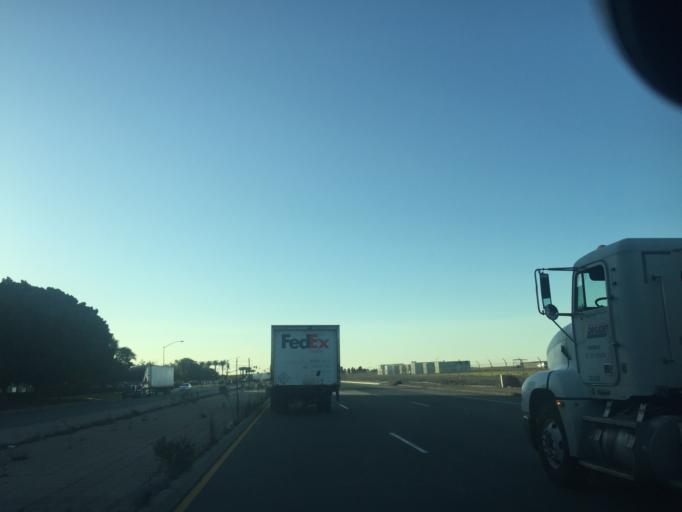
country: MX
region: Baja California
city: Tijuana
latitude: 32.5680
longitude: -116.9764
